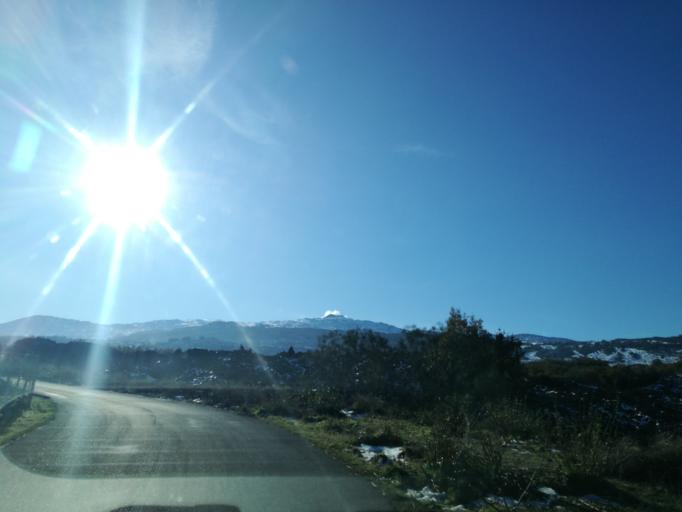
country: IT
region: Sicily
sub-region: Catania
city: Randazzo
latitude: 37.8616
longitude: 14.9795
